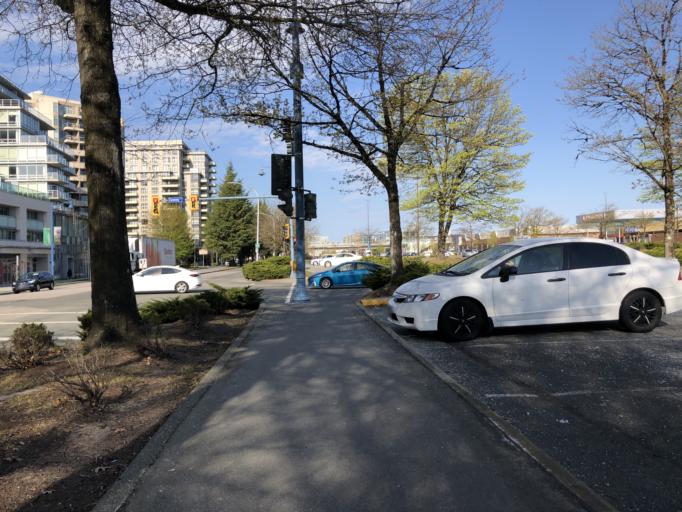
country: CA
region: British Columbia
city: Richmond
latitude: 49.1740
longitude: -123.1309
